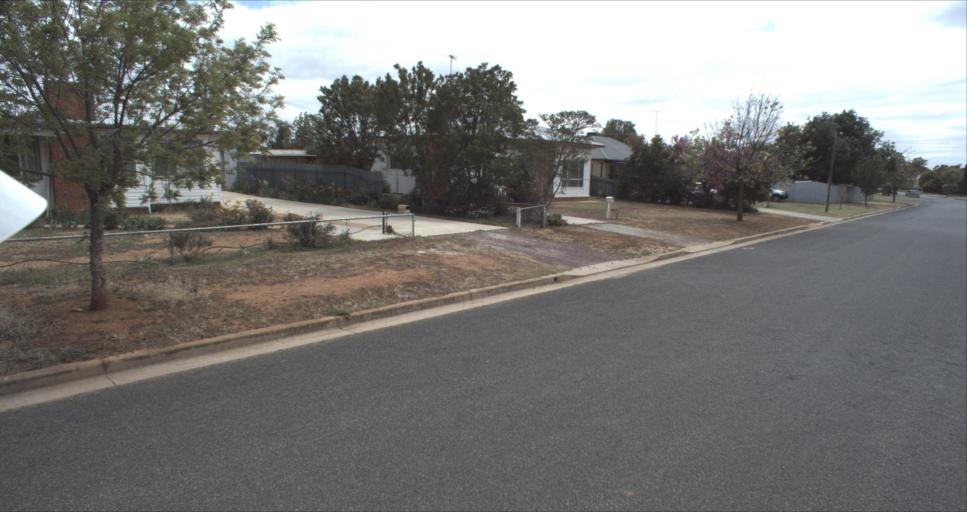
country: AU
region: New South Wales
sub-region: Leeton
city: Leeton
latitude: -34.5605
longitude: 146.3995
